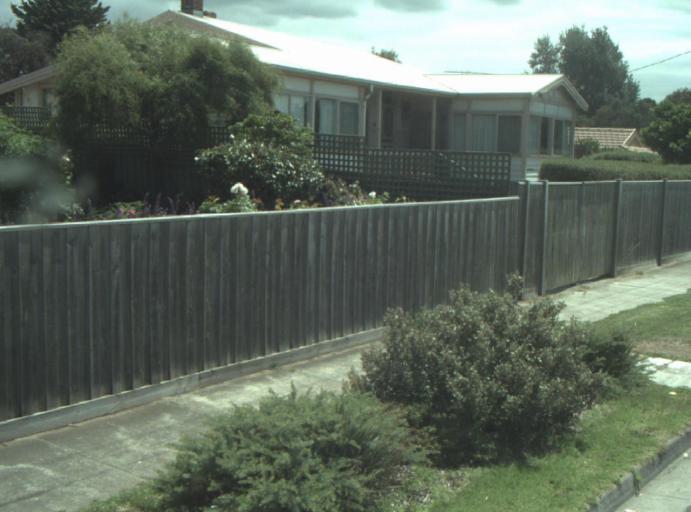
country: AU
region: Victoria
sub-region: Greater Geelong
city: Leopold
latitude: -38.2812
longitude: 144.4940
